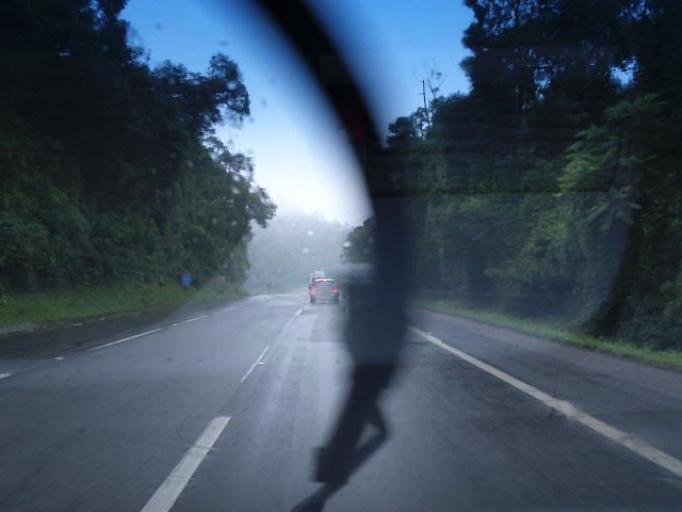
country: BR
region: Parana
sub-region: Antonina
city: Antonina
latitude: -25.1123
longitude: -48.7567
